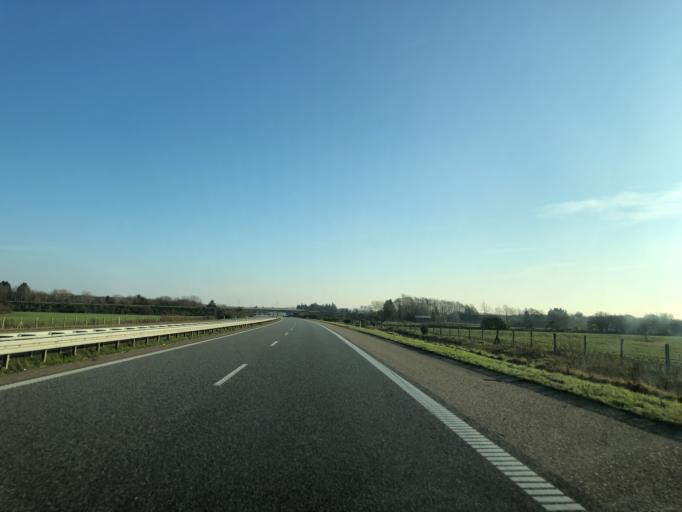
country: DK
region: South Denmark
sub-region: Vejle Kommune
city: Give
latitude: 55.8774
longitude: 9.2337
